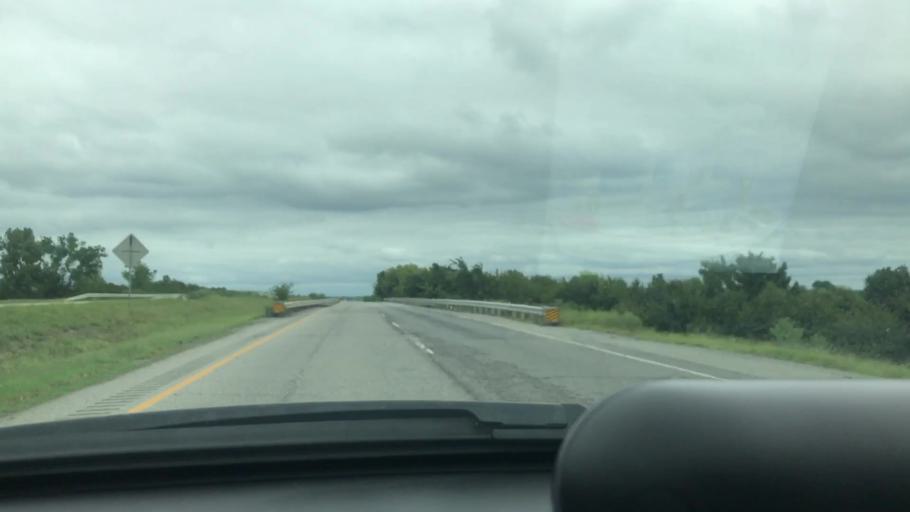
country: US
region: Oklahoma
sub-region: Wagoner County
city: Wagoner
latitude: 35.9785
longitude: -95.3813
